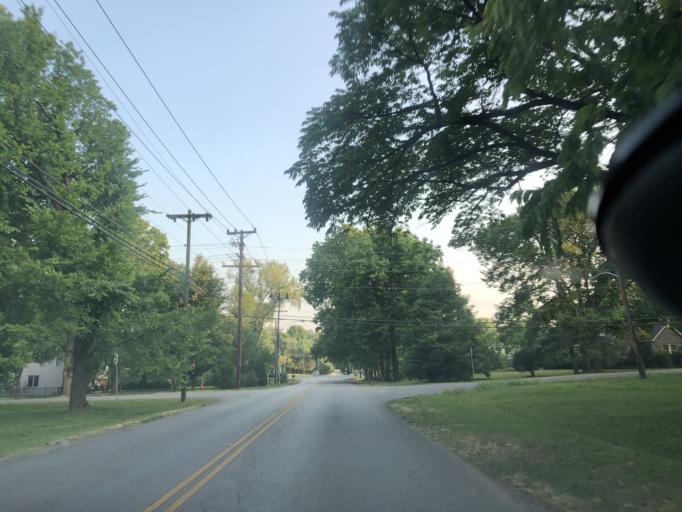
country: US
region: Tennessee
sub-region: Davidson County
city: Oak Hill
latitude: 36.1126
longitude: -86.7870
